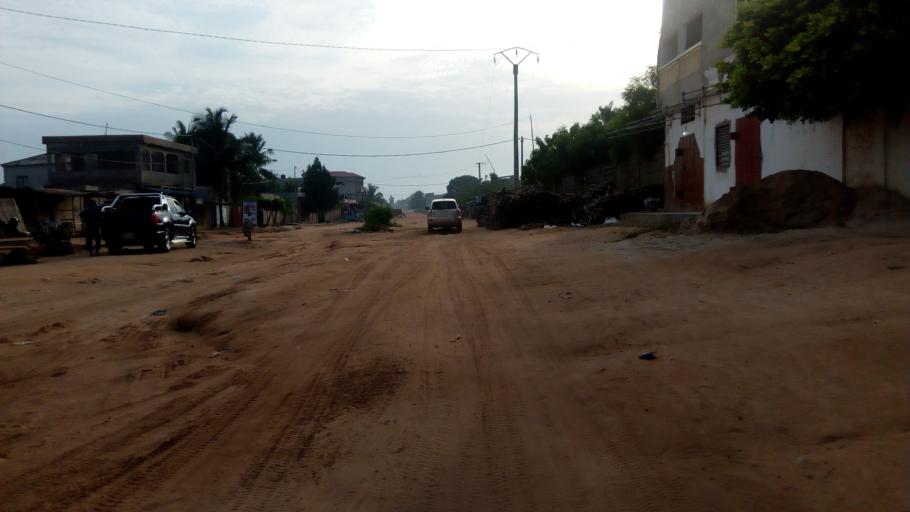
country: TG
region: Maritime
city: Lome
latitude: 6.1789
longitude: 1.1491
